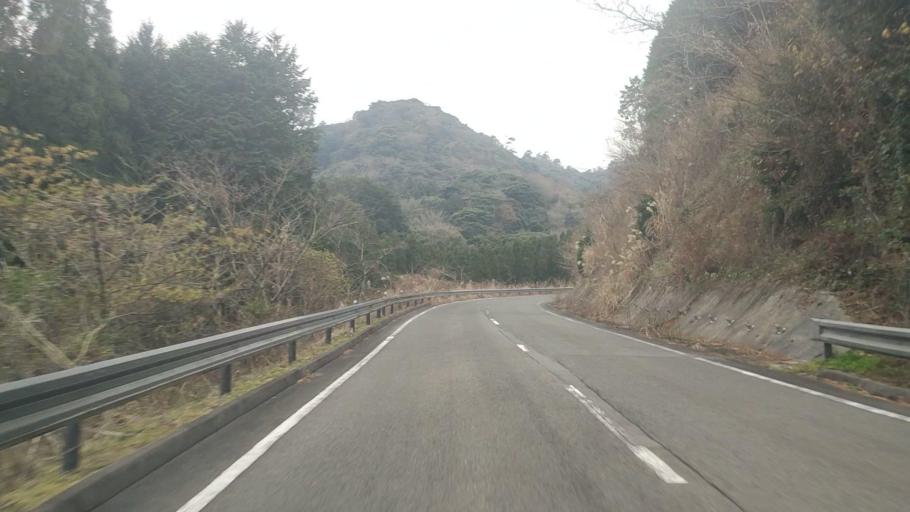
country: JP
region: Nagasaki
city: Shimabara
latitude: 32.7845
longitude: 130.2820
